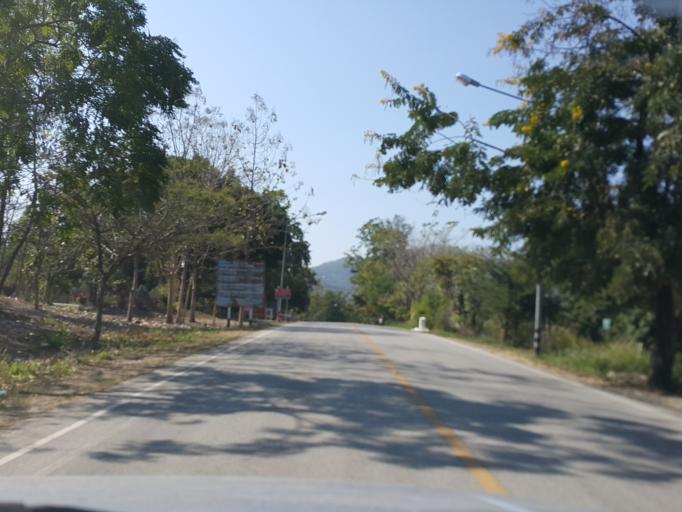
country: TH
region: Chiang Mai
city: Mae Wang
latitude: 18.6159
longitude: 98.7761
